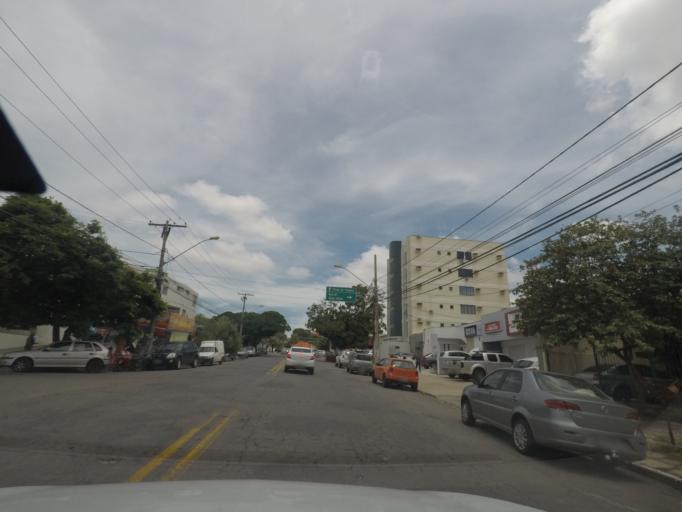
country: BR
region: Goias
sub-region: Goiania
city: Goiania
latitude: -16.6888
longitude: -49.2513
